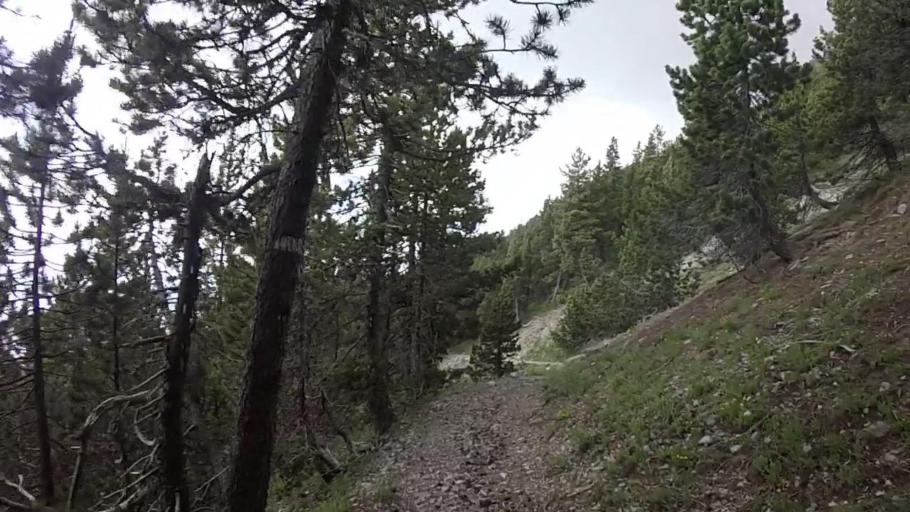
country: FR
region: Provence-Alpes-Cote d'Azur
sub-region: Departement des Alpes-de-Haute-Provence
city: Seyne-les-Alpes
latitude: 44.3996
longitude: 6.3815
